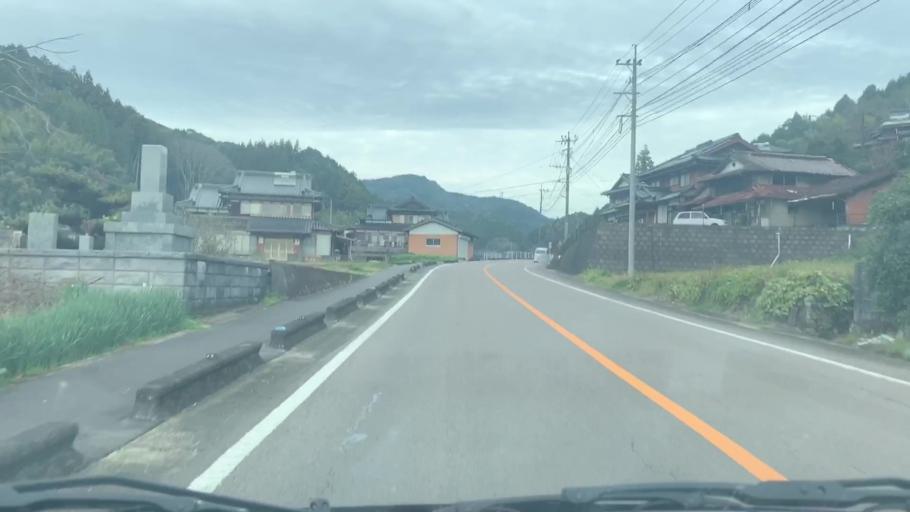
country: JP
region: Saga Prefecture
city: Ureshinomachi-shimojuku
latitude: 33.1528
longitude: 129.9732
